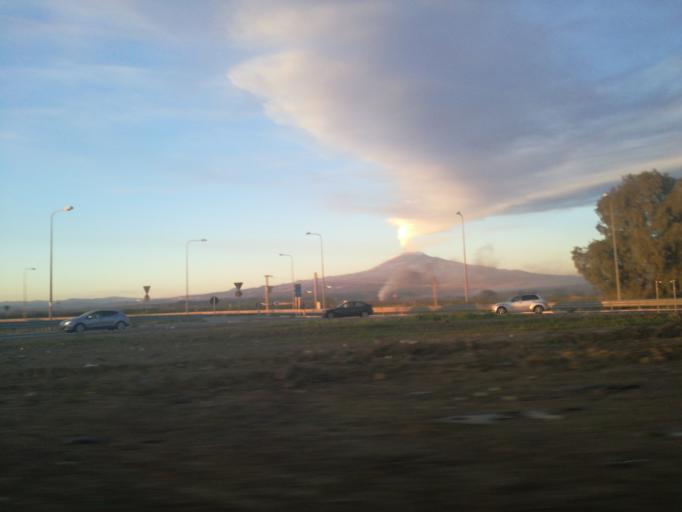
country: IT
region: Sicily
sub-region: Catania
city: Motta Sant'Anastasia
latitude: 37.4290
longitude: 14.9357
